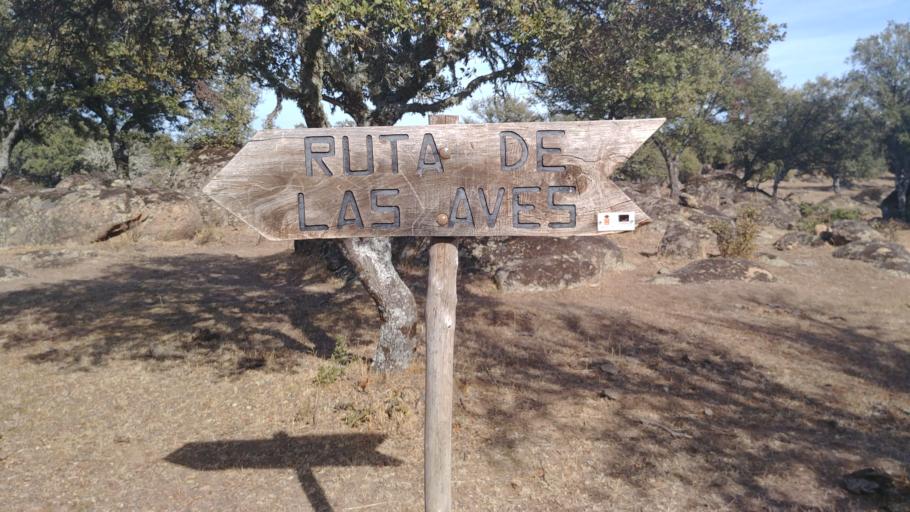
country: ES
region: Castille-La Mancha
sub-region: Province of Toledo
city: Navalcan
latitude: 40.0623
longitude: -5.1414
